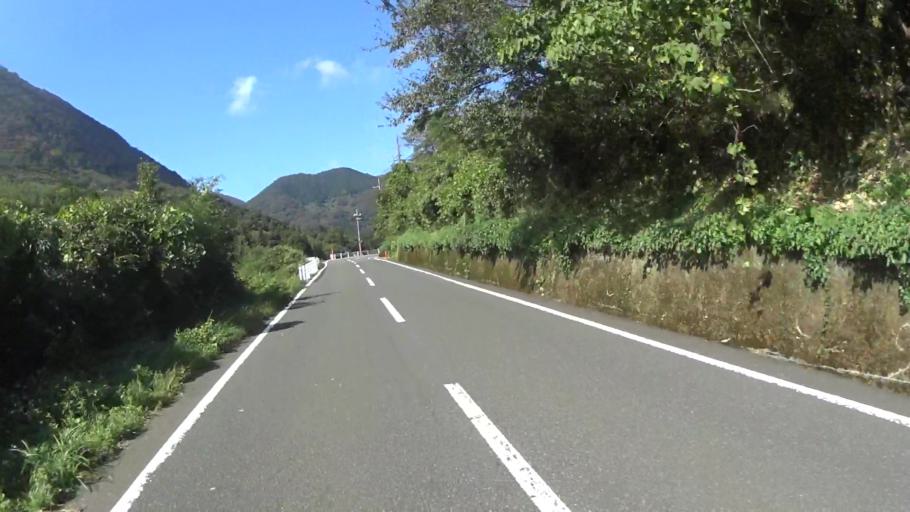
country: JP
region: Kyoto
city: Miyazu
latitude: 35.7395
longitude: 135.2463
